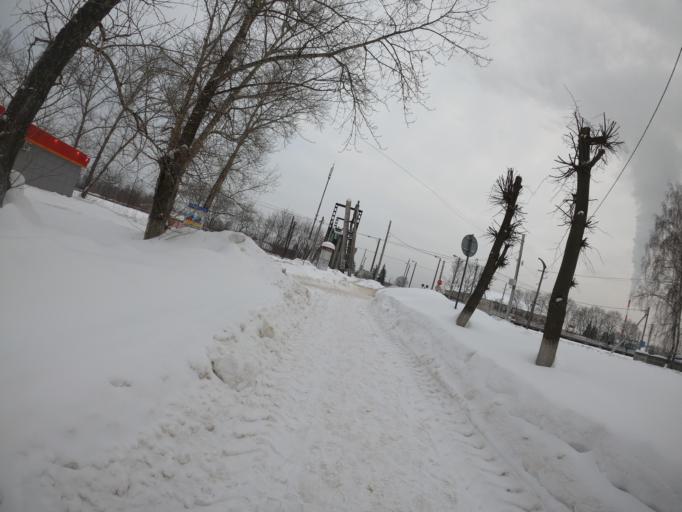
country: RU
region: Moskovskaya
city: Elektrogorsk
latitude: 55.8660
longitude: 38.7836
